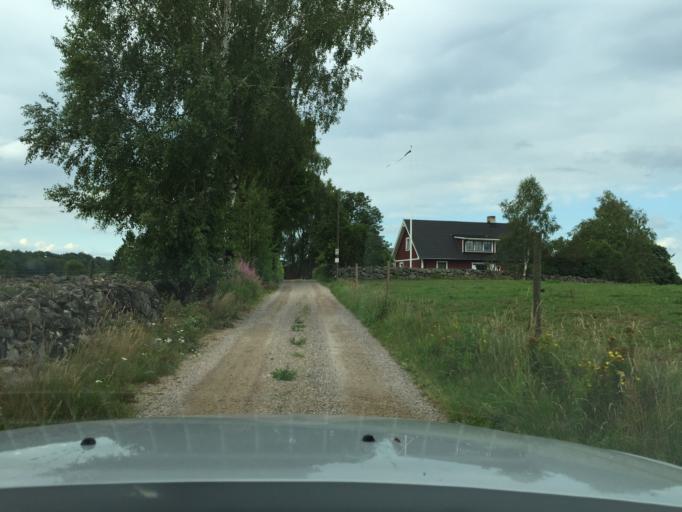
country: SE
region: Skane
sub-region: Hassleholms Kommun
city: Sosdala
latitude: 56.0512
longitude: 13.6899
